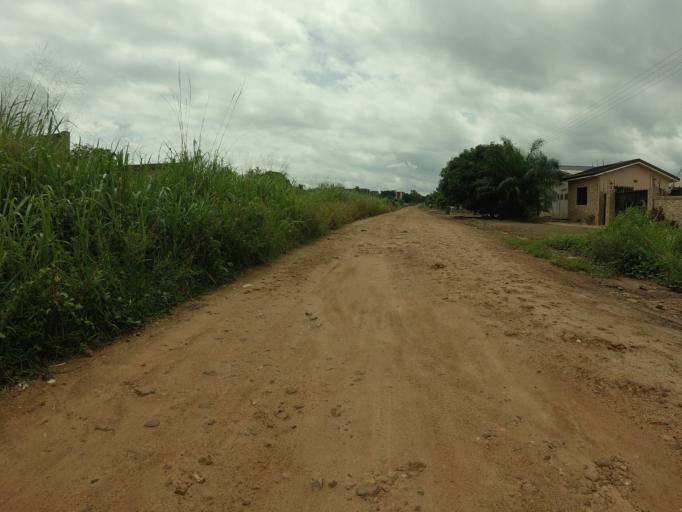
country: GH
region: Volta
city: Ho
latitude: 6.5866
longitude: 0.4607
